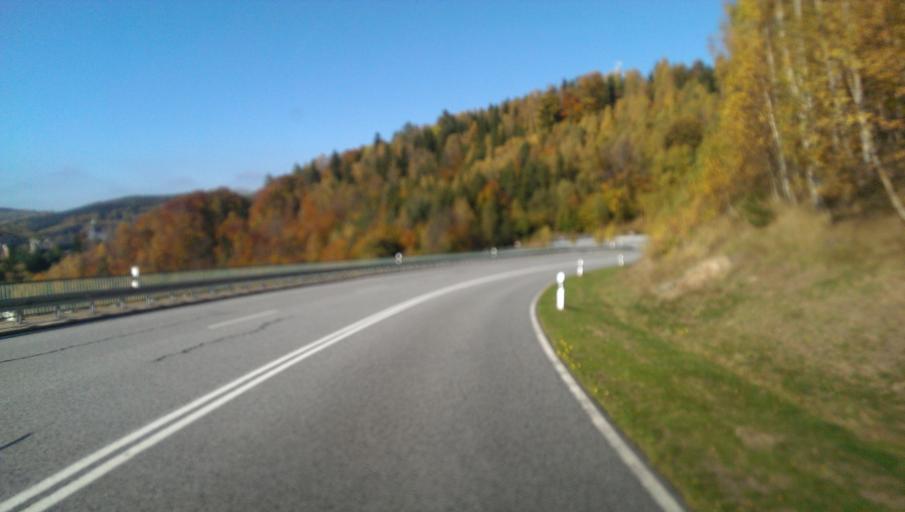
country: DE
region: Saxony
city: Barenstein
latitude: 50.7820
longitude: 13.8333
